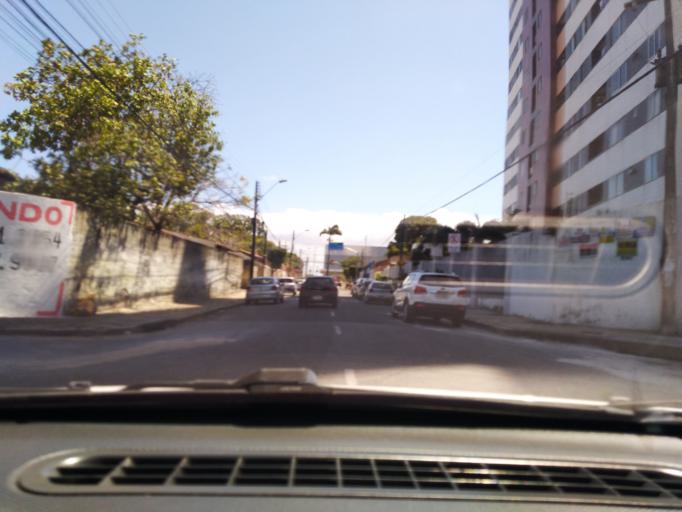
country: BR
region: Ceara
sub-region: Eusebio
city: Eusebio
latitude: -3.8134
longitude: -38.4979
